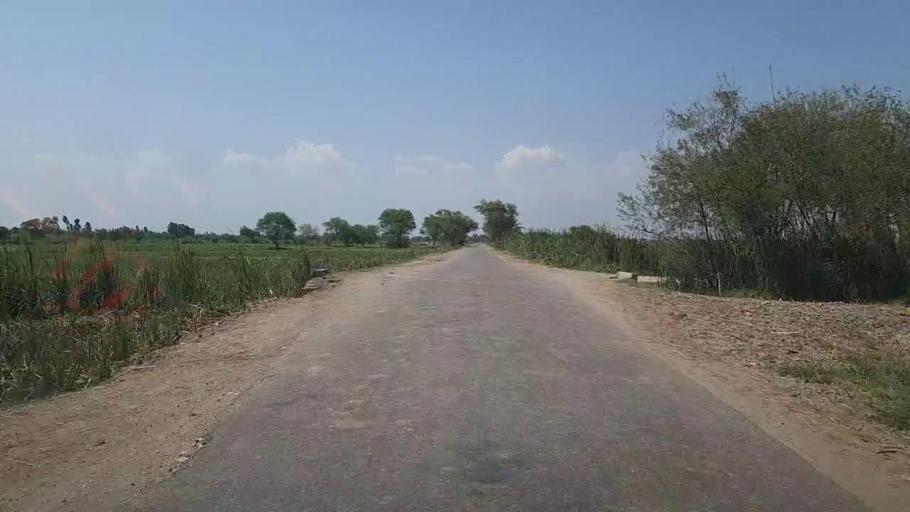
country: PK
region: Sindh
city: Khairpur
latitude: 28.0741
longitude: 69.6398
